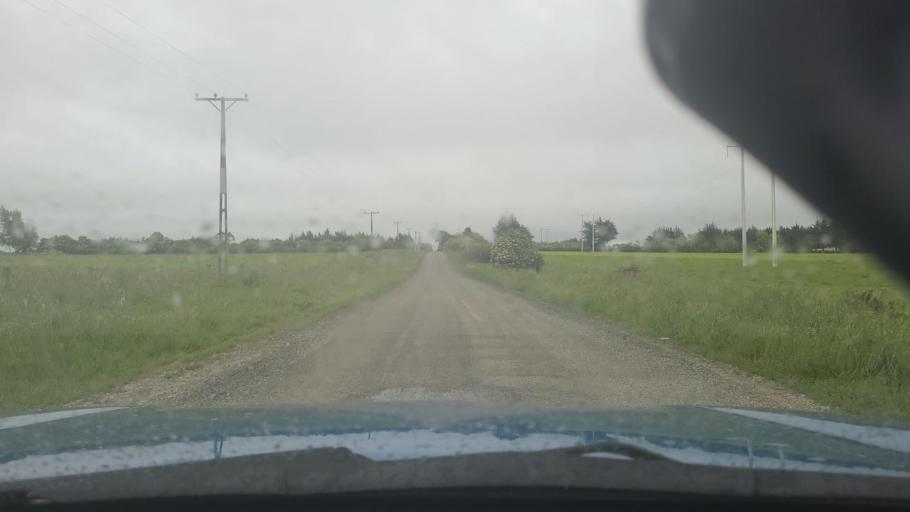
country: NZ
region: Southland
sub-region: Invercargill City
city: Invercargill
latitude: -46.3452
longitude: 168.5417
